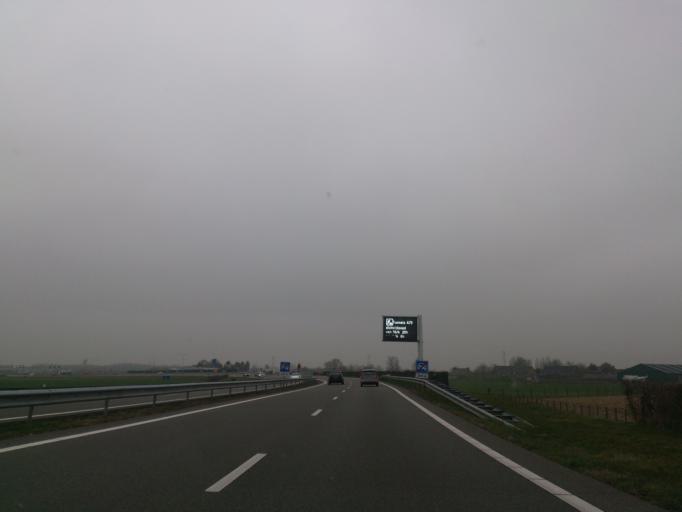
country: NL
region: Limburg
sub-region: Gemeente Roermond
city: Leeuwen
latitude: 51.2047
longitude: 6.0341
